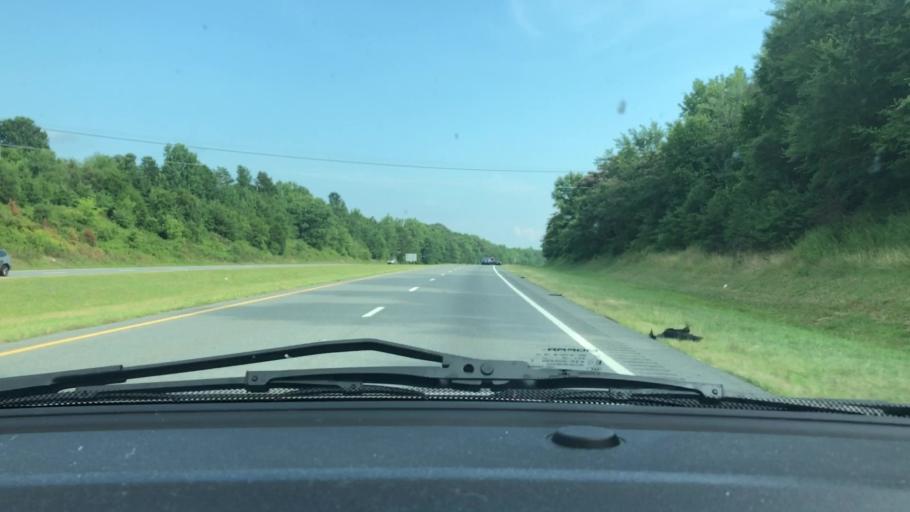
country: US
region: North Carolina
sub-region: Guilford County
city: Forest Oaks
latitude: 35.9540
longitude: -79.6932
